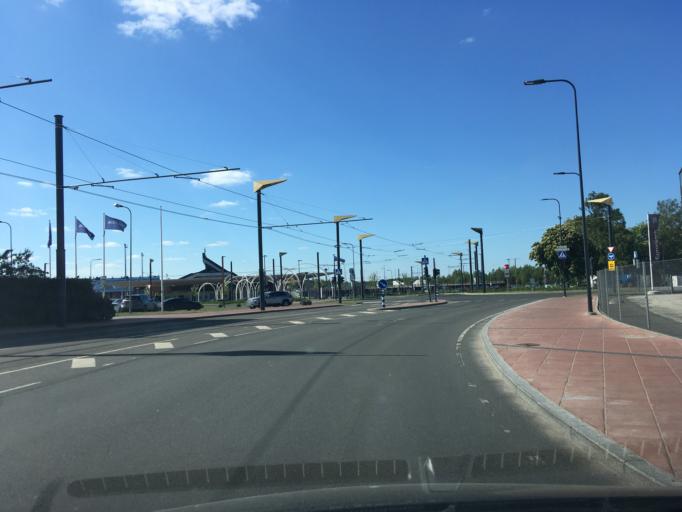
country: EE
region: Harju
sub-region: Tallinna linn
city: Tallinn
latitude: 59.4197
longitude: 24.7994
